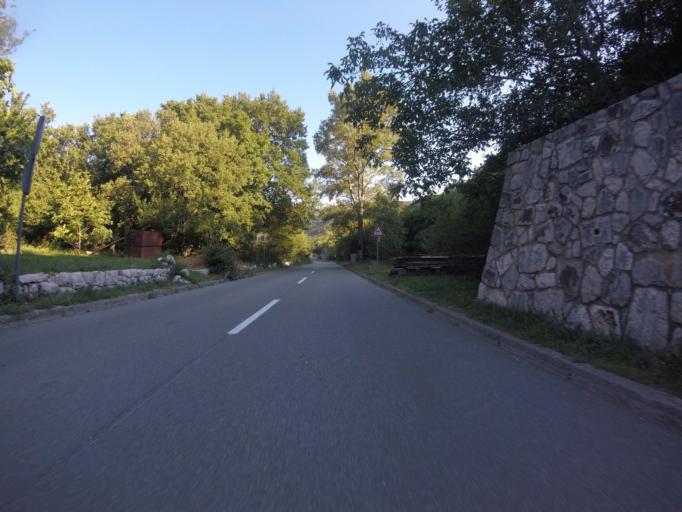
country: HR
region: Primorsko-Goranska
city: Hreljin
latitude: 45.2597
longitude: 14.6115
